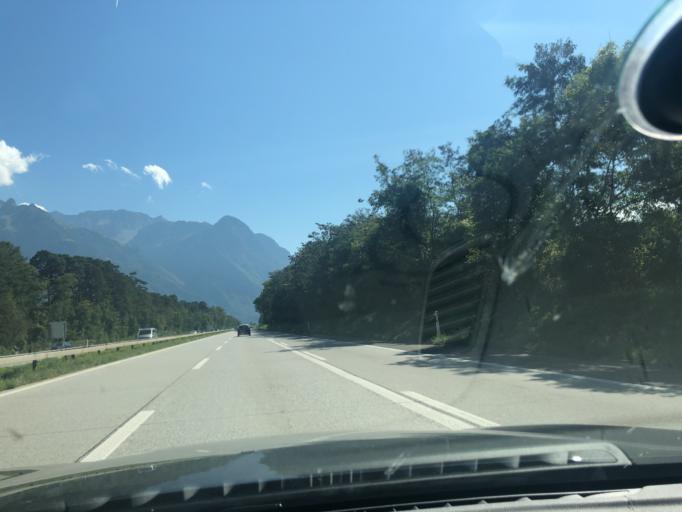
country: LI
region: Vaduz
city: Vaduz
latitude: 47.1288
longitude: 9.5104
